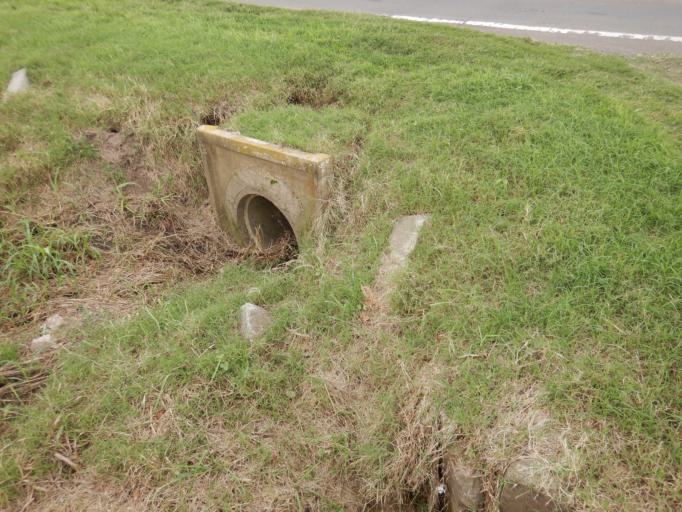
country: AR
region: Santa Fe
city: Carcarana
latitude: -32.8712
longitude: -61.1016
